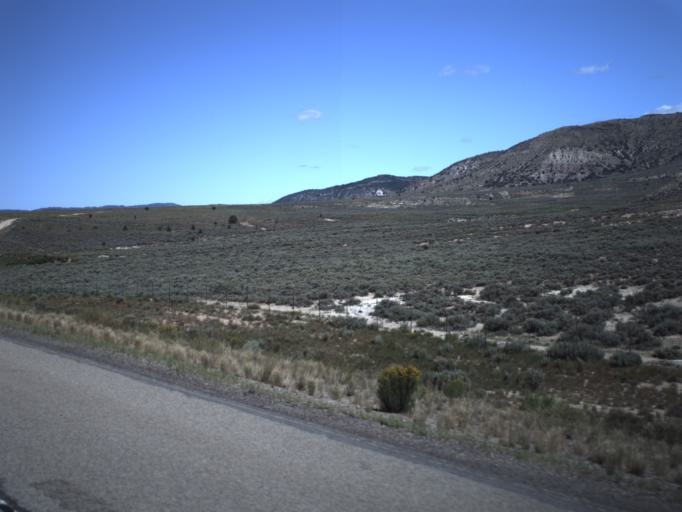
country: US
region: Utah
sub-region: Carbon County
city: Helper
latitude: 39.8563
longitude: -111.0190
